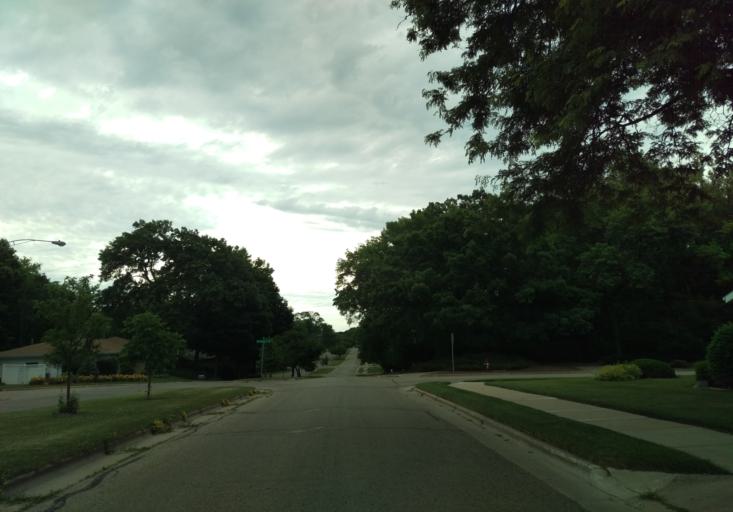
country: US
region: Wisconsin
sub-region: Dane County
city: Shorewood Hills
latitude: 43.0680
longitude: -89.4740
